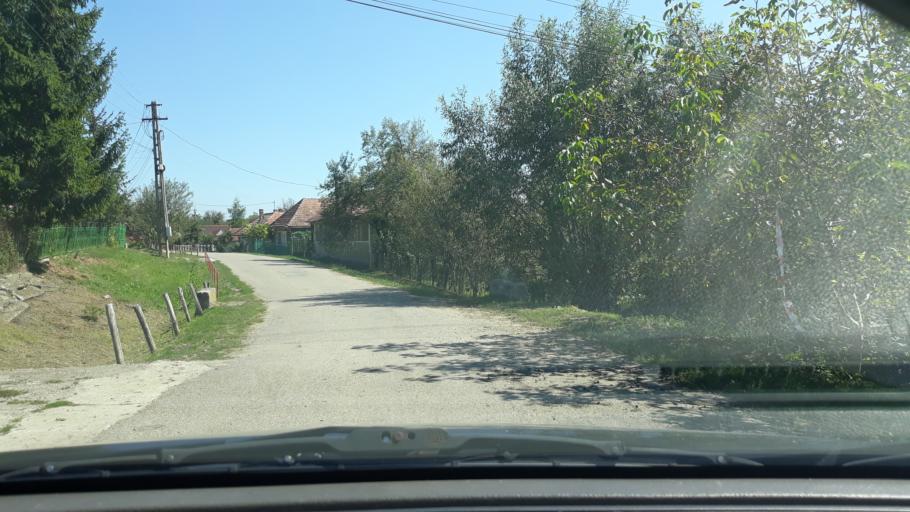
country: RO
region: Salaj
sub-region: Comuna Dobrin
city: Dobrin
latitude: 47.2970
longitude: 23.0897
